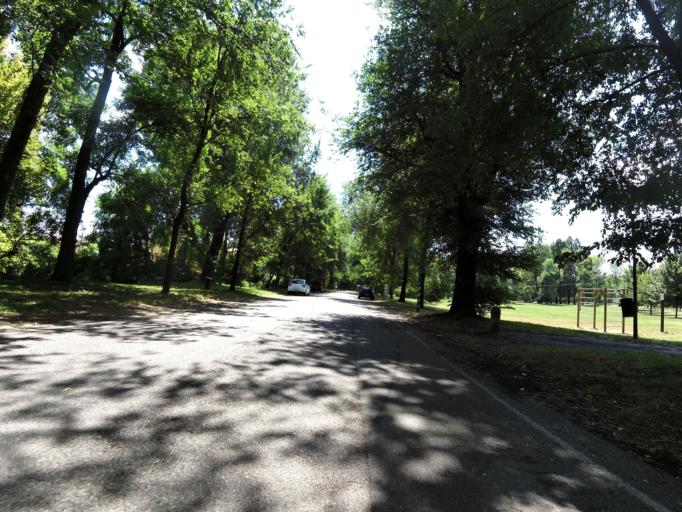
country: IT
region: Lombardy
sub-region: Citta metropolitana di Milano
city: Vimodrone
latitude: 45.4994
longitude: 9.2531
